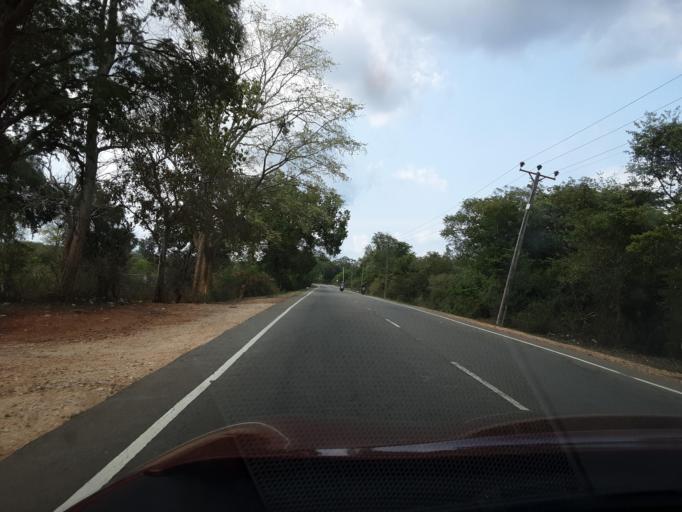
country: LK
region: Uva
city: Haputale
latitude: 6.5026
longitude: 81.1315
